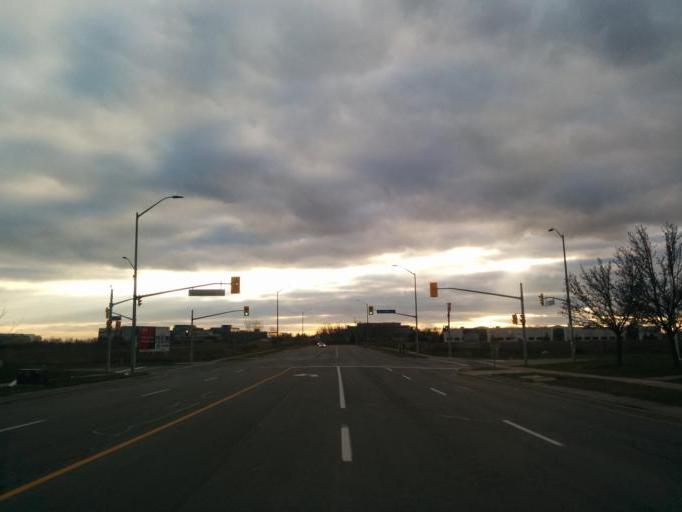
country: CA
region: Ontario
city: Etobicoke
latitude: 43.6553
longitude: -79.6073
